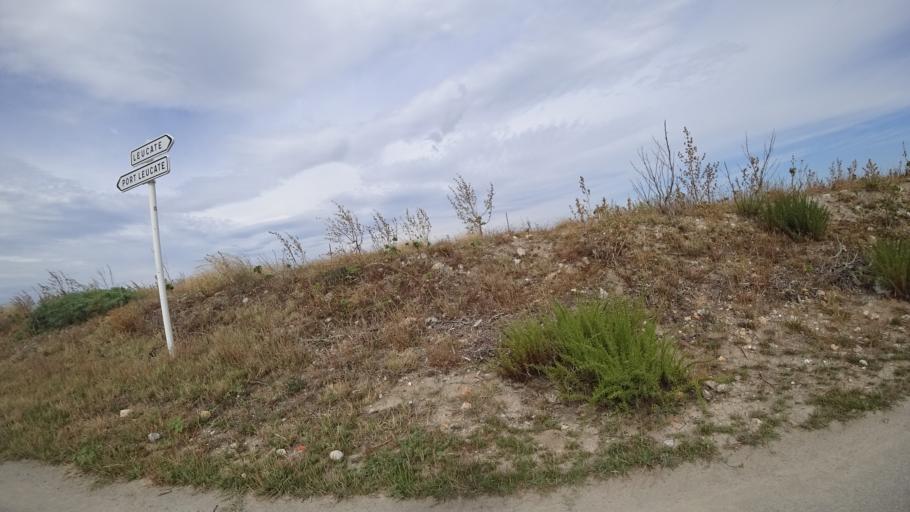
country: FR
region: Languedoc-Roussillon
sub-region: Departement de l'Aude
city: Leucate
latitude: 42.8871
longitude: 3.0502
